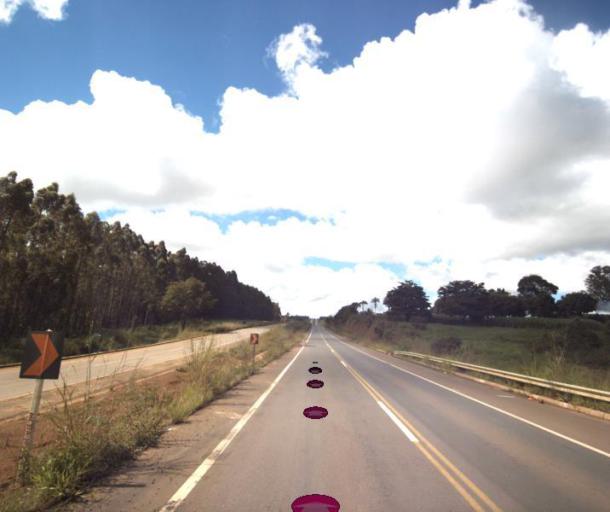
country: BR
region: Goias
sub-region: Anapolis
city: Anapolis
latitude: -16.2087
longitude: -49.0197
